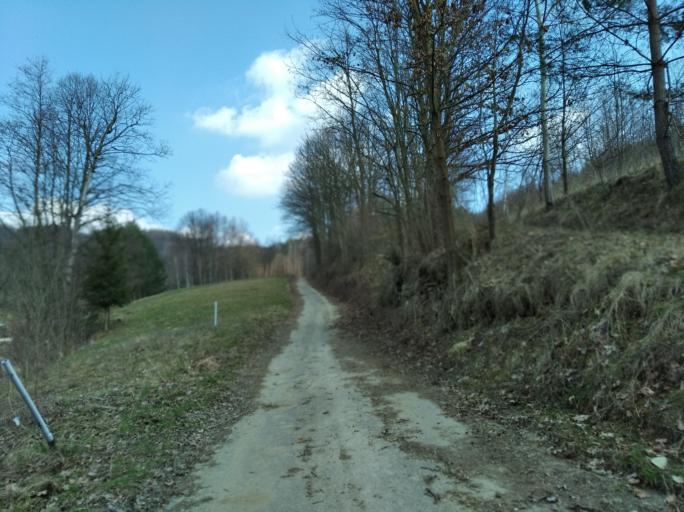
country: PL
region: Subcarpathian Voivodeship
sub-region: Powiat strzyzowski
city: Strzyzow
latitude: 49.8417
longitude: 21.8380
